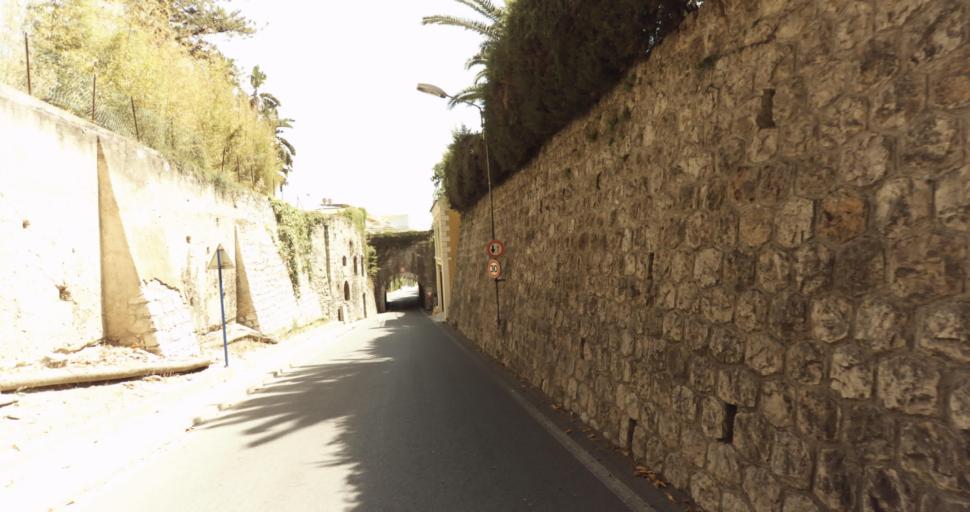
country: FR
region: Provence-Alpes-Cote d'Azur
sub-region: Departement des Alpes-Maritimes
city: Menton
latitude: 43.7854
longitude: 7.5158
